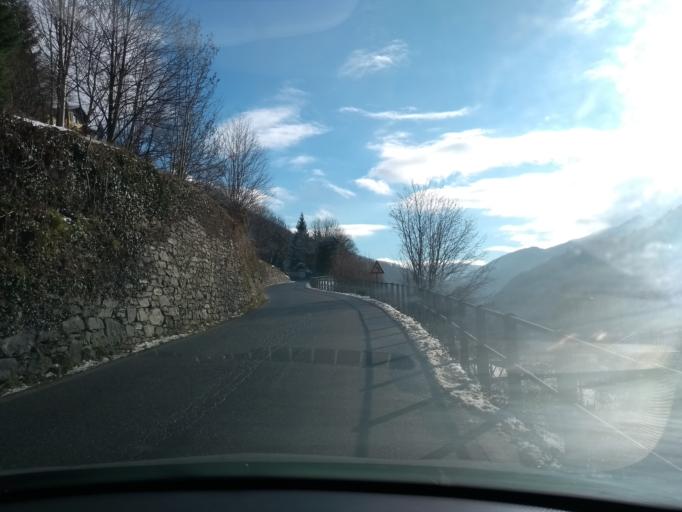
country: IT
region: Piedmont
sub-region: Provincia di Torino
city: Ceres
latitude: 45.3113
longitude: 7.3905
